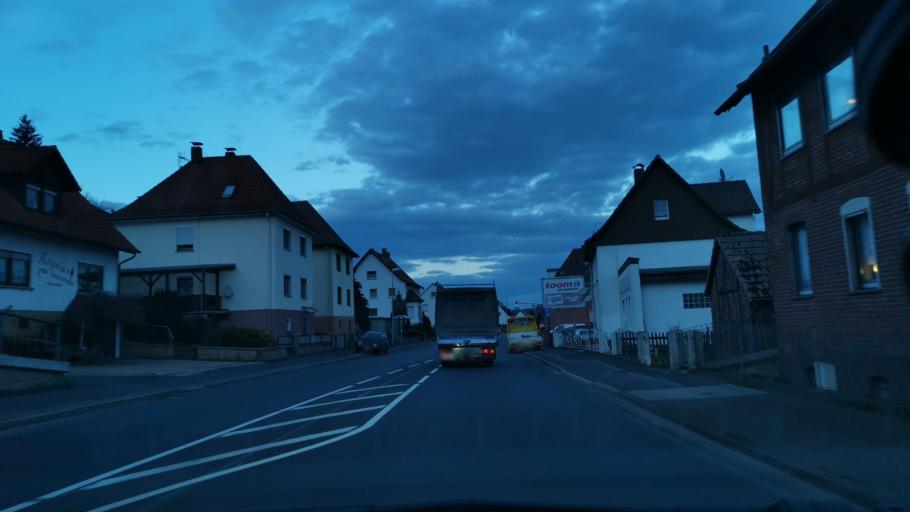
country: DE
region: Hesse
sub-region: Regierungsbezirk Kassel
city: Bad Hersfeld
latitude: 50.8946
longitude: 9.7387
